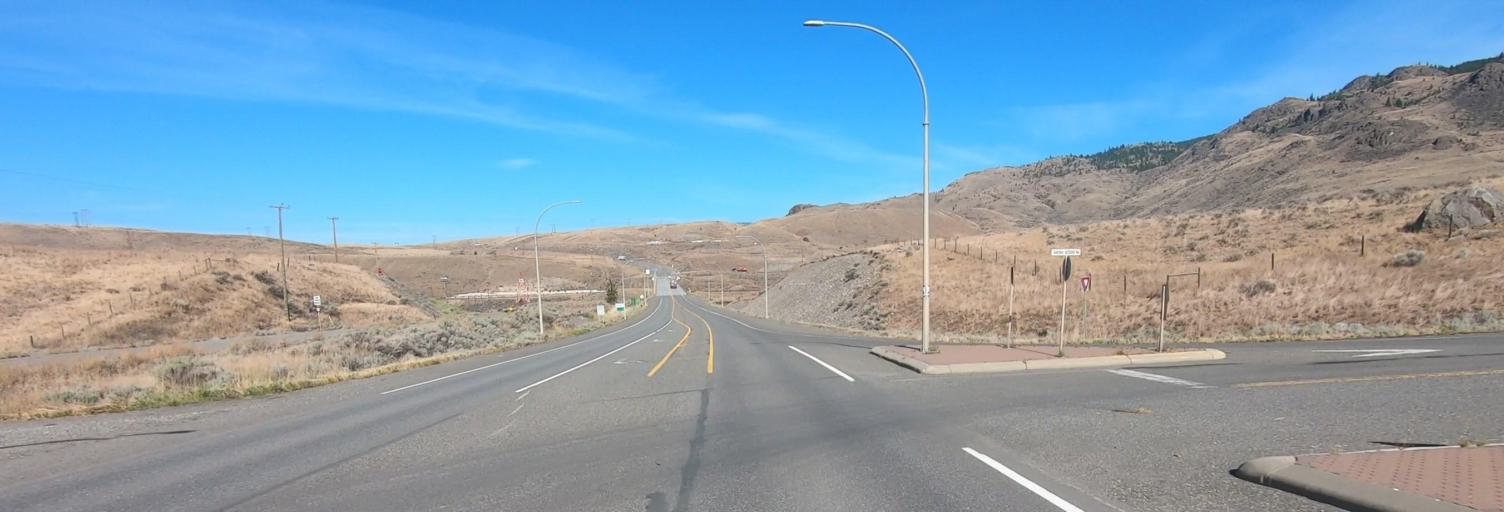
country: CA
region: British Columbia
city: Logan Lake
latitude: 50.7546
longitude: -120.8673
